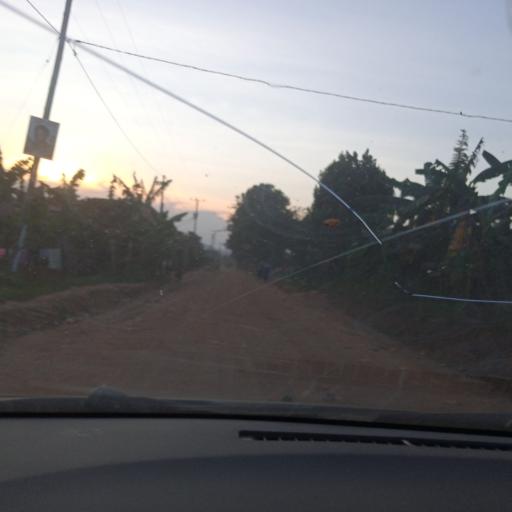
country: UG
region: Central Region
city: Masaka
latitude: -0.3117
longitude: 31.7659
